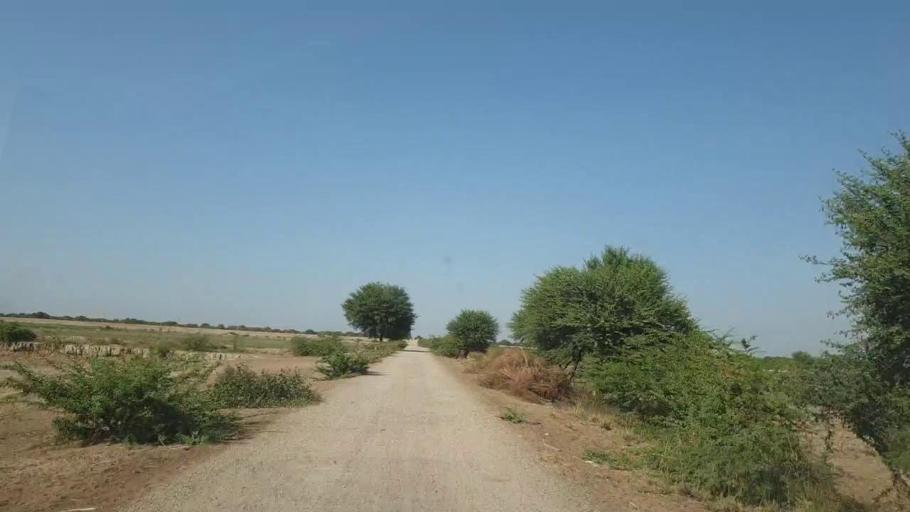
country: PK
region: Sindh
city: Nabisar
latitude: 25.0288
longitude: 69.4866
